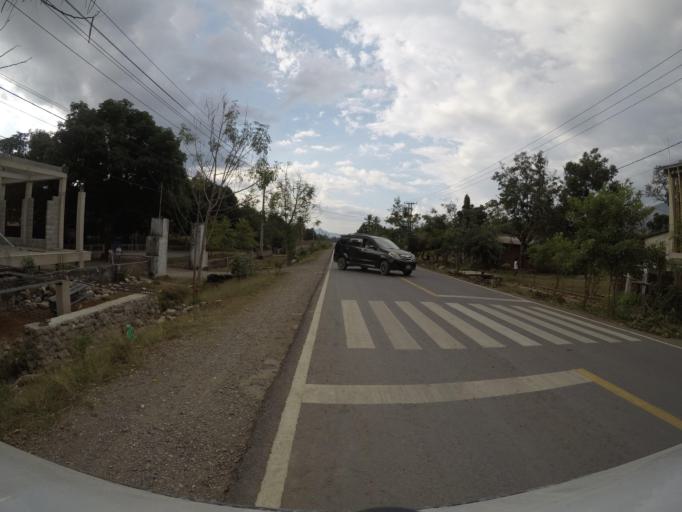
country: TL
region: Bobonaro
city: Maliana
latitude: -8.9779
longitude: 125.2202
